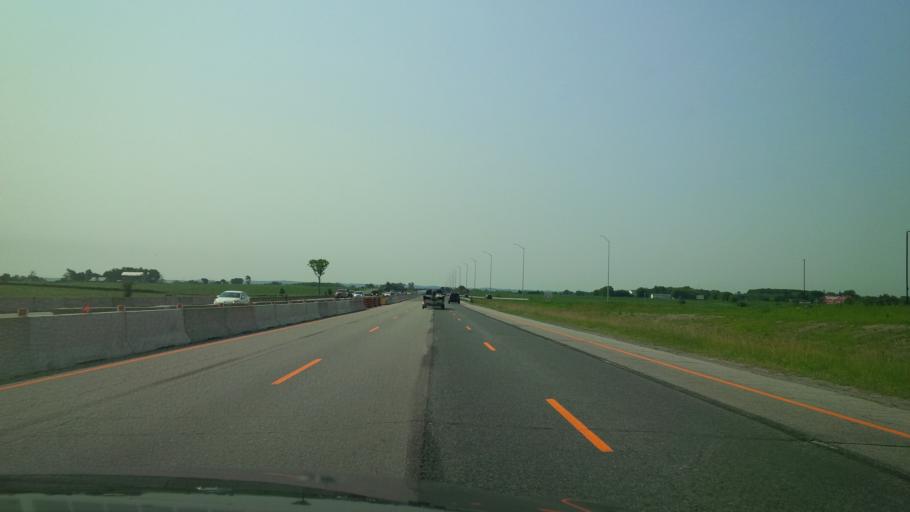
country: CA
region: Ontario
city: Innisfil
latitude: 44.2461
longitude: -79.6694
